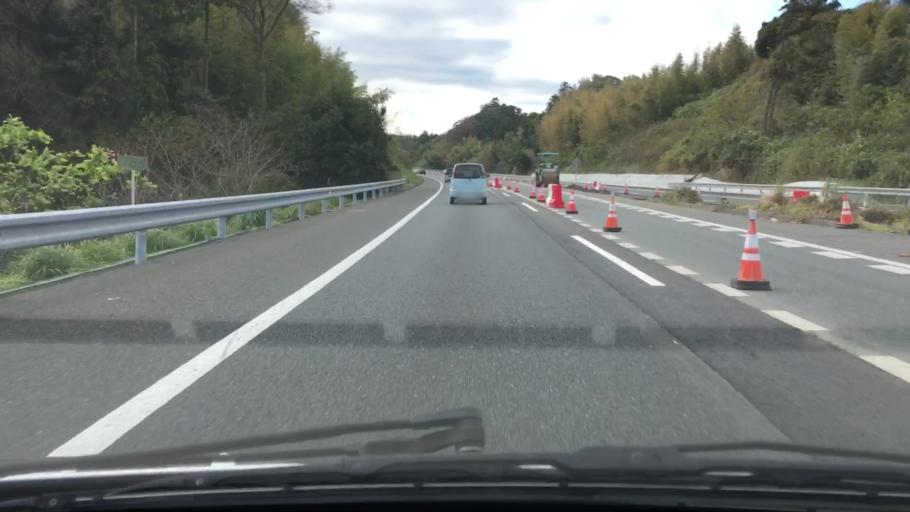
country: JP
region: Chiba
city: Kimitsu
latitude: 35.2610
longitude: 139.8973
